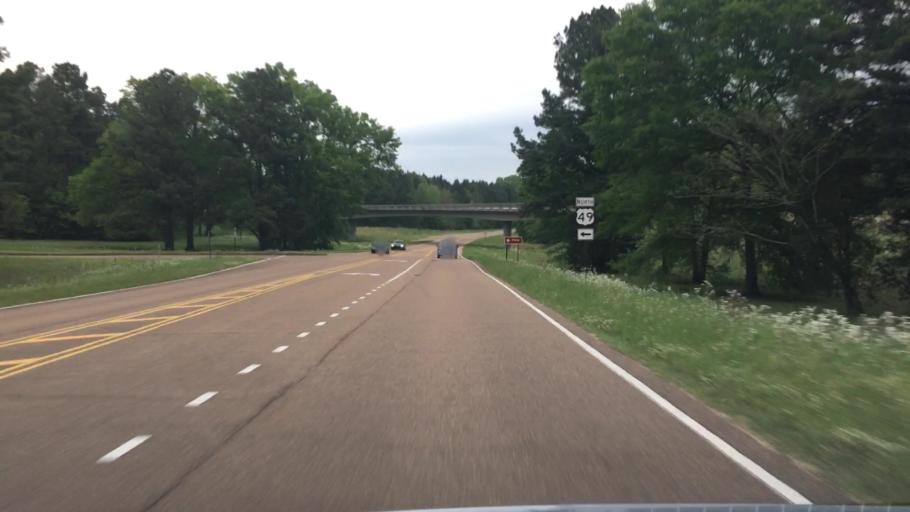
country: US
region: Mississippi
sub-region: Hinds County
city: Clinton
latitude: 32.3837
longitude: -90.2583
